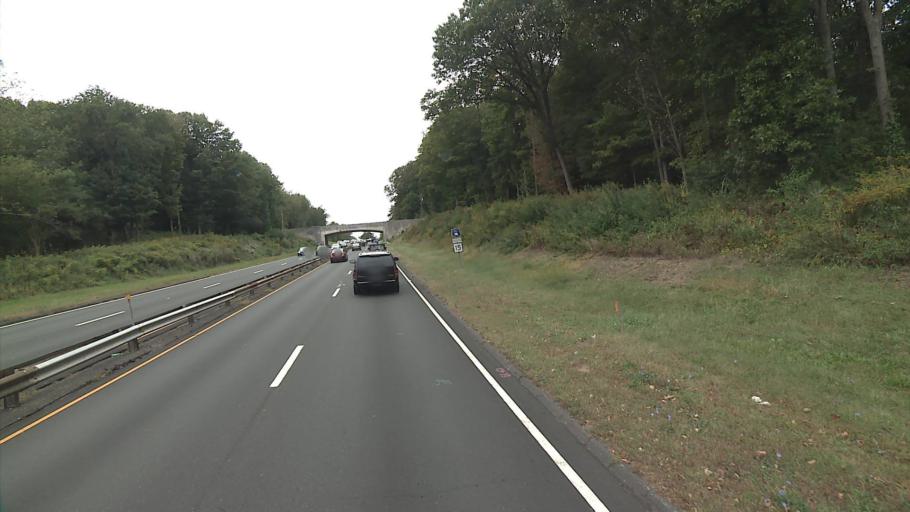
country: US
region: Connecticut
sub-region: Fairfield County
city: Norwalk
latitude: 41.1381
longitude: -73.4432
